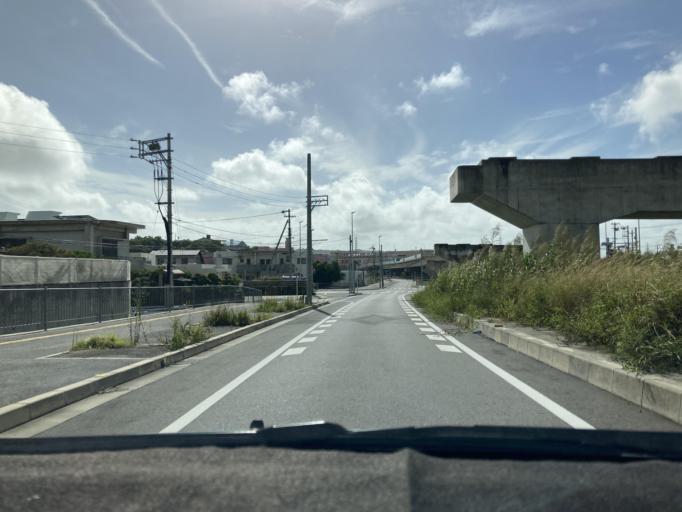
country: JP
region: Okinawa
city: Naha-shi
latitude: 26.2049
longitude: 127.7337
